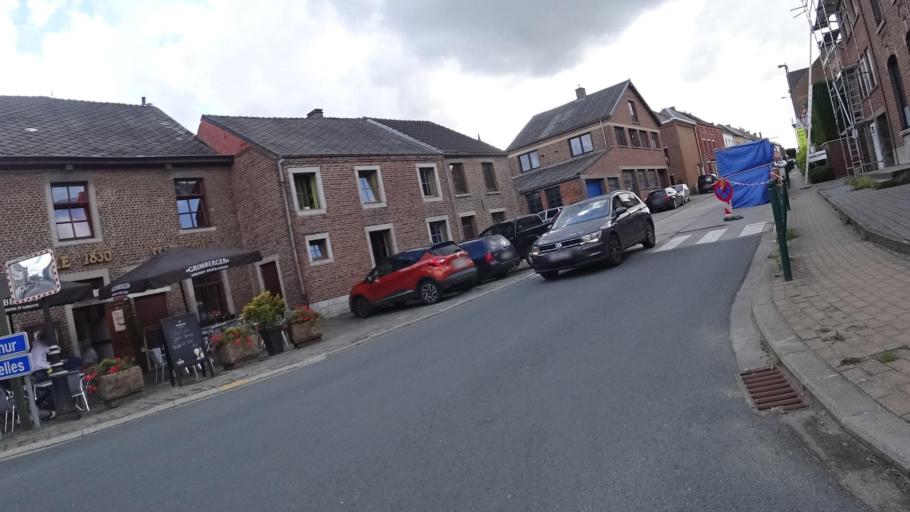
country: BE
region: Wallonia
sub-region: Province du Brabant Wallon
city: Villers-la-Ville
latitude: 50.5464
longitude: 4.5350
